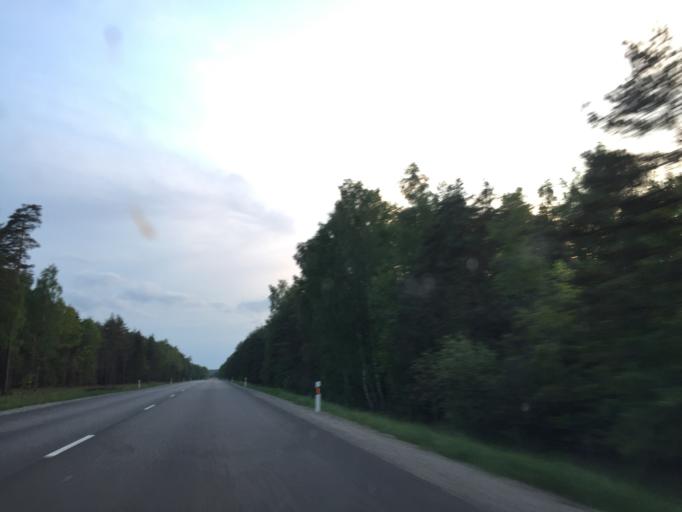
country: LT
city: Venta
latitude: 56.0007
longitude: 22.5710
